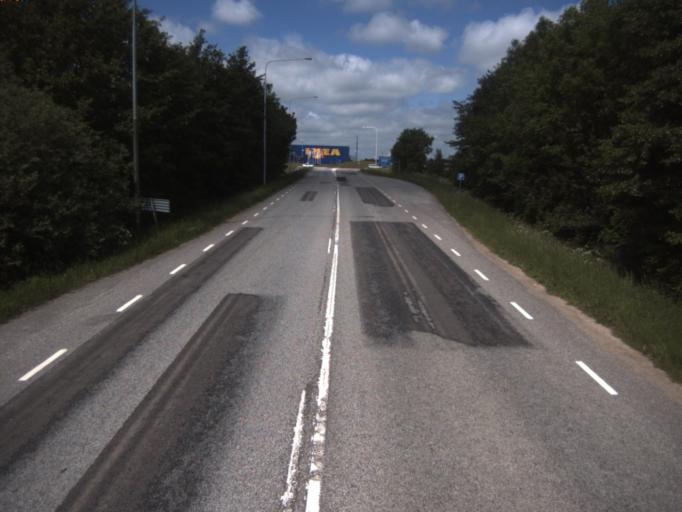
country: SE
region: Skane
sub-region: Helsingborg
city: Odakra
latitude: 56.0890
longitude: 12.7650
